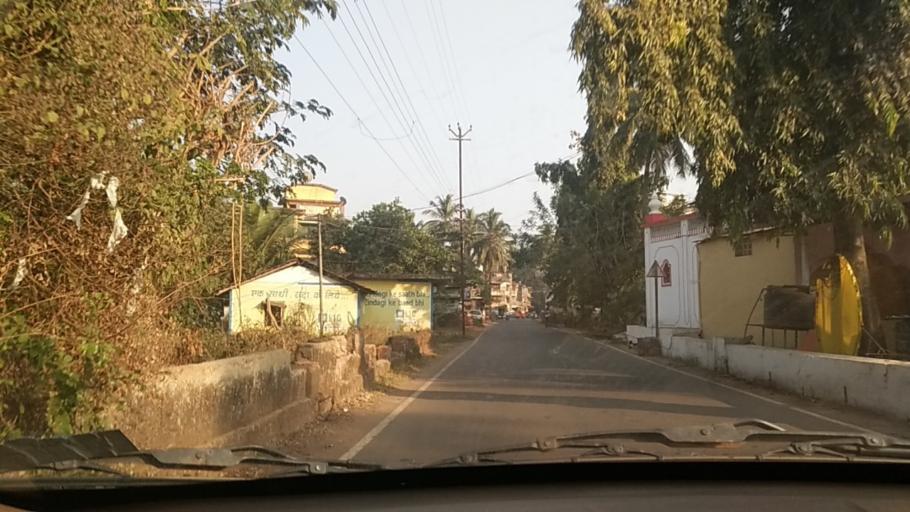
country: IN
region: Goa
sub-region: North Goa
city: Bambolim
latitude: 15.4809
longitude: 73.8560
